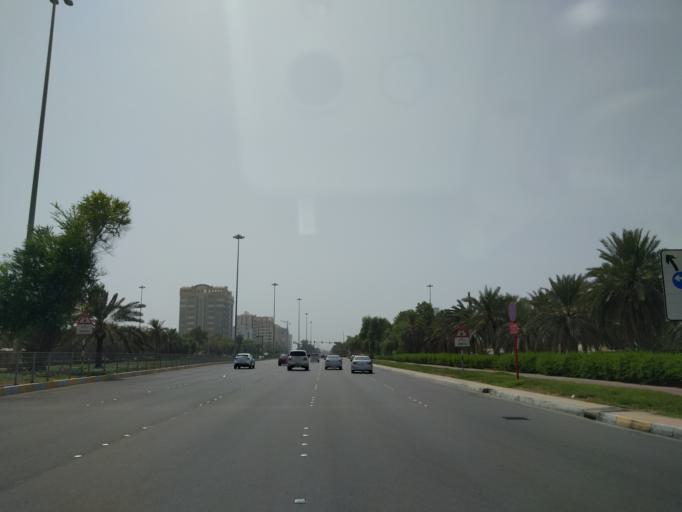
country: AE
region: Abu Dhabi
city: Abu Dhabi
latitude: 24.4370
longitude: 54.4186
